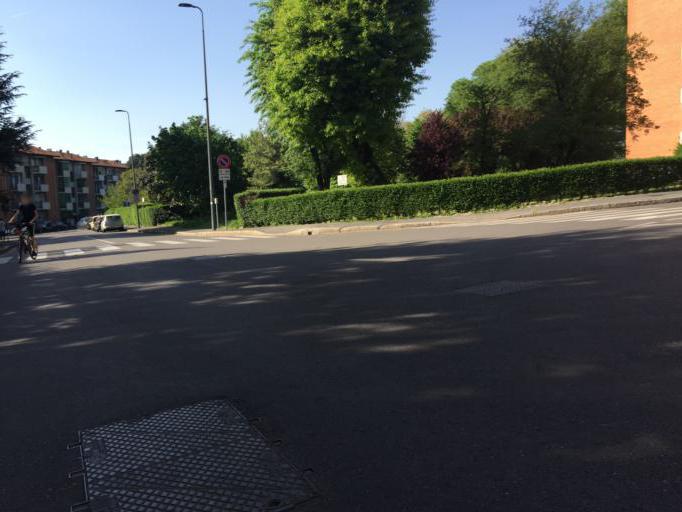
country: IT
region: Lombardy
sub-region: Citta metropolitana di Milano
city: Linate
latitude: 45.4602
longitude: 9.2466
